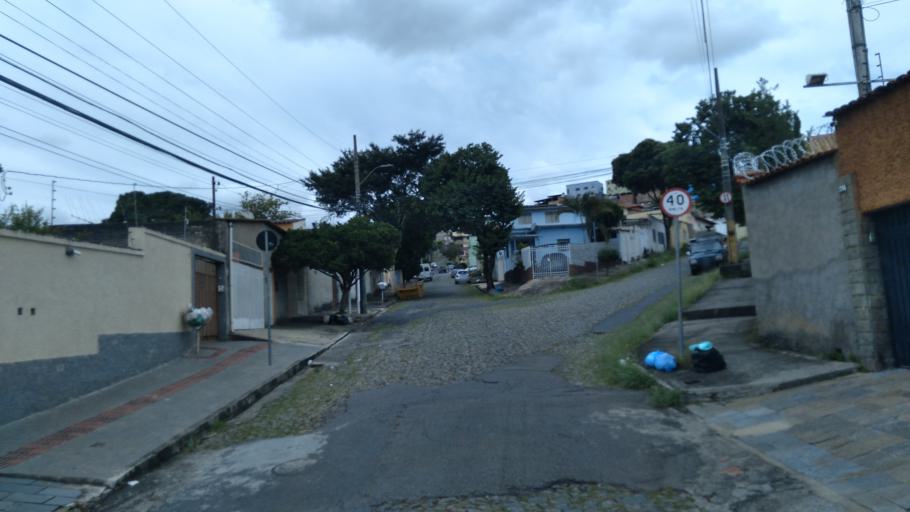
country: BR
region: Minas Gerais
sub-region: Contagem
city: Contagem
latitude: -19.9089
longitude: -44.0049
